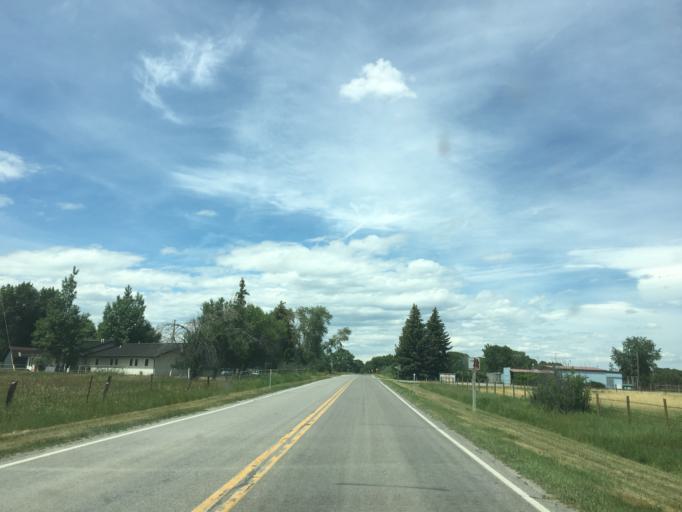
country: US
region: Montana
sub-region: Teton County
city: Choteau
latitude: 47.8266
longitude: -112.1952
